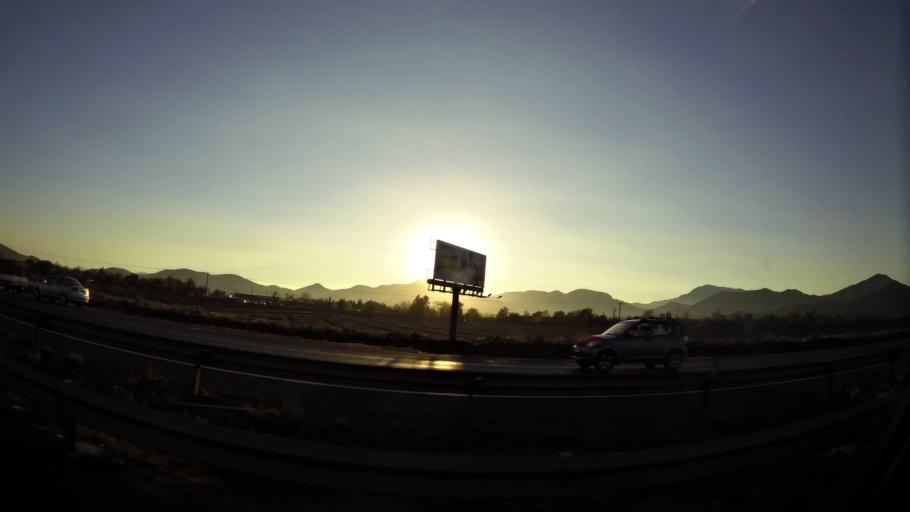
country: CL
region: Santiago Metropolitan
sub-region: Provincia de Santiago
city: Lo Prado
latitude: -33.5135
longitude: -70.7992
